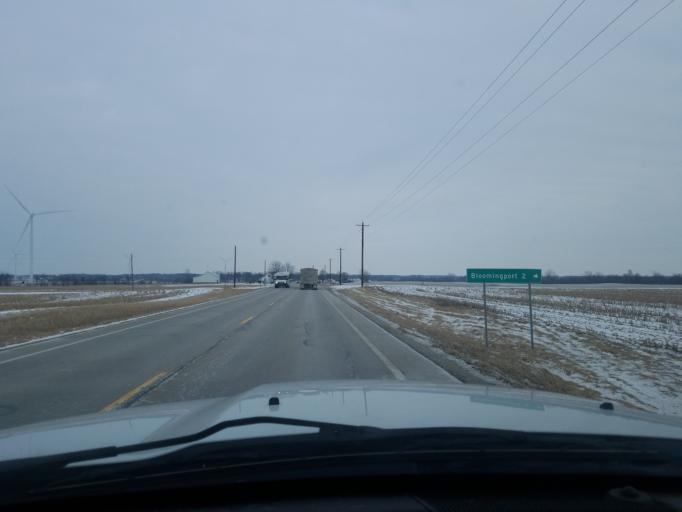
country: US
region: Indiana
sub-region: Randolph County
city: Lynn
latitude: 40.0486
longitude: -84.9929
